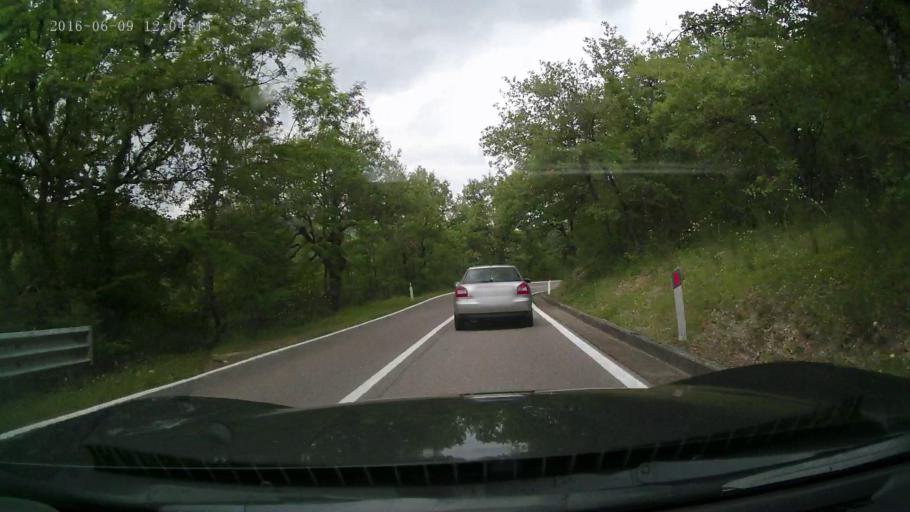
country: IT
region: Tuscany
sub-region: Province of Florence
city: Panzano in Chianti
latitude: 43.5199
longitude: 11.2948
